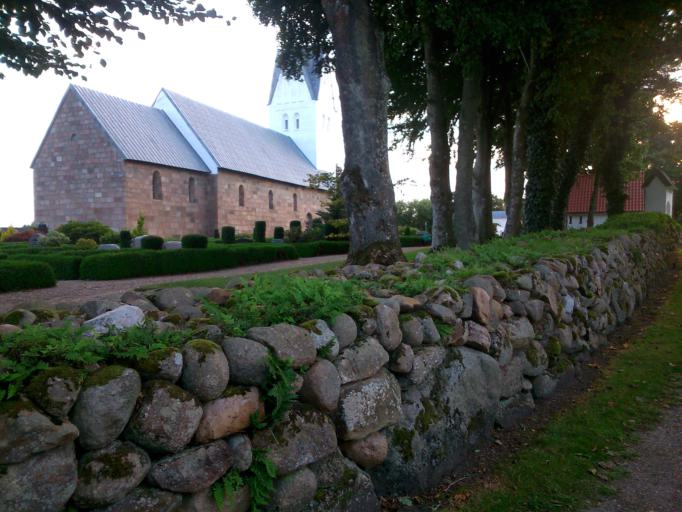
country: DK
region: Central Jutland
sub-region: Ringkobing-Skjern Kommune
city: Tarm
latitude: 55.9554
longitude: 8.6567
